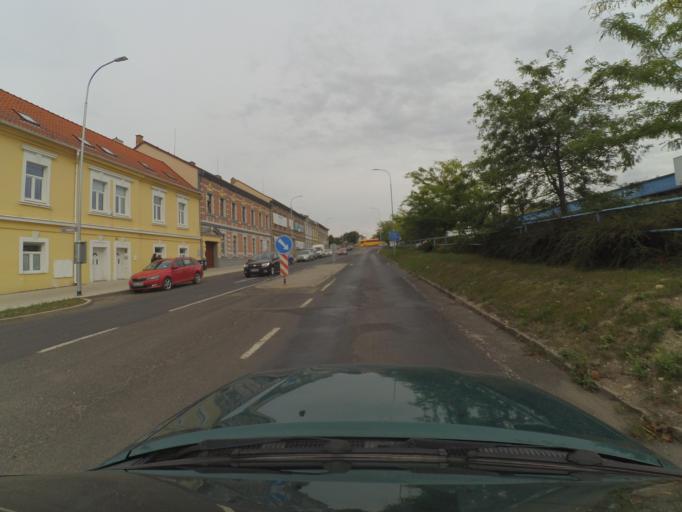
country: CZ
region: Ustecky
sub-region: Okres Louny
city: Louny
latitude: 50.3553
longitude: 13.8051
